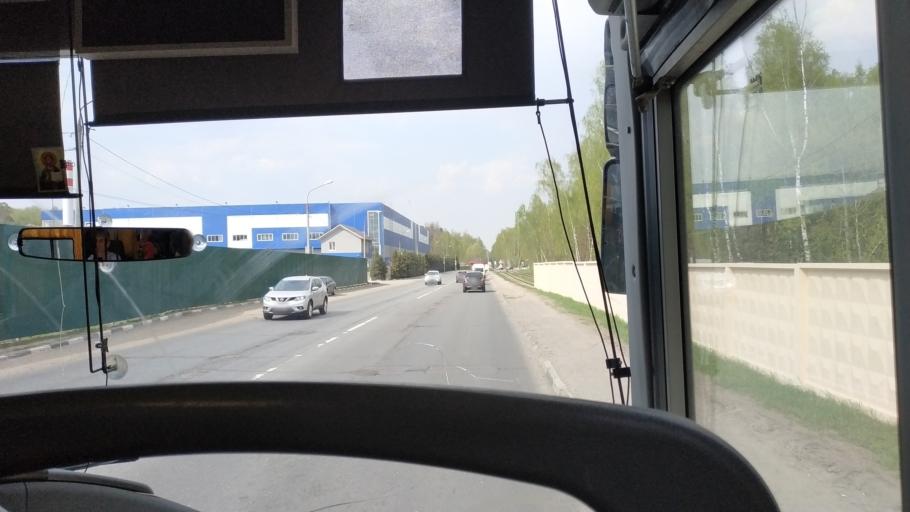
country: RU
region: Moskovskaya
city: Lytkarino
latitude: 55.5896
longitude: 37.9152
